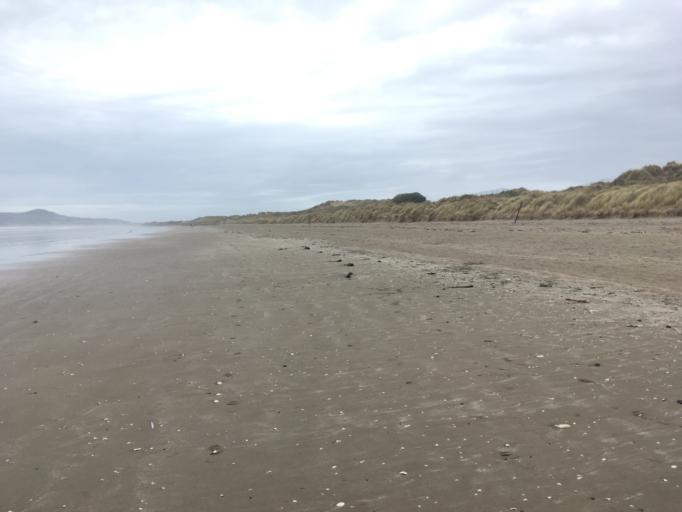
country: IE
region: Leinster
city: Portmarnock
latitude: 53.4226
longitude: -6.1220
